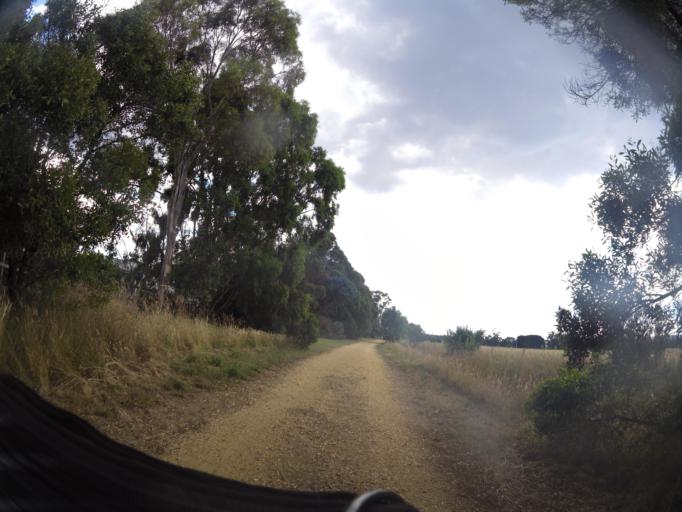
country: AU
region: Victoria
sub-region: Wellington
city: Heyfield
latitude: -38.0122
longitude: 146.6959
